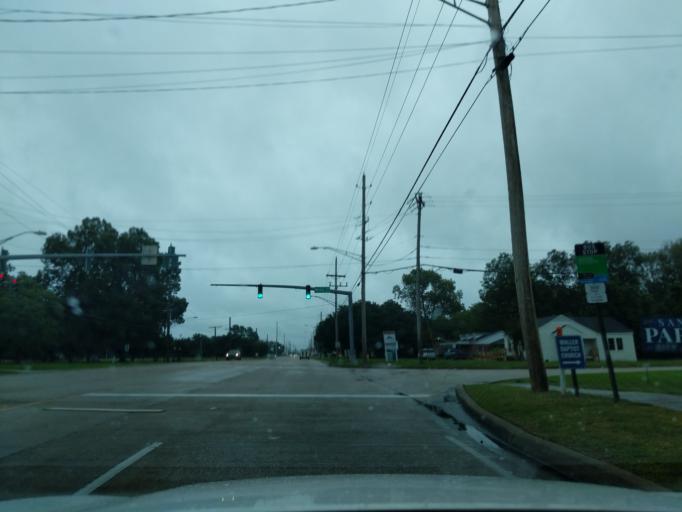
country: US
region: Louisiana
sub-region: Bossier Parish
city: Bossier City
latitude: 32.5200
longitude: -93.7012
